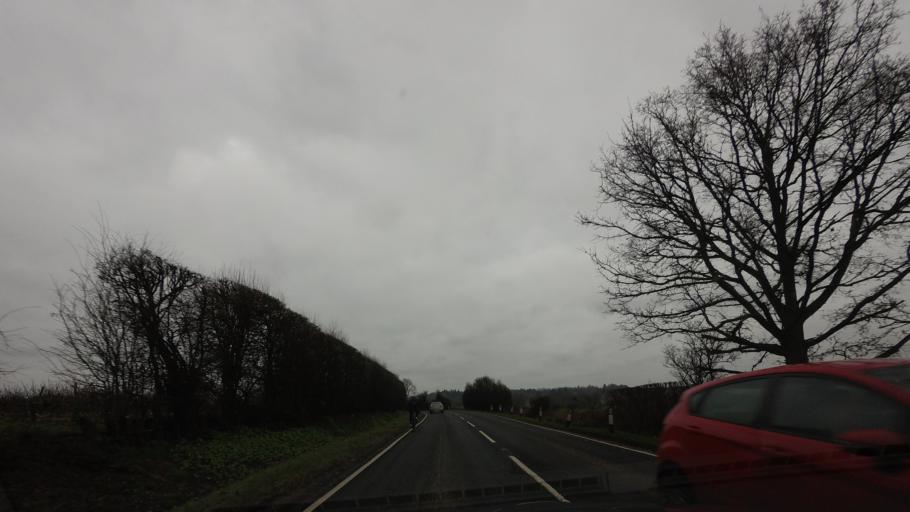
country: GB
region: England
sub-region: Kent
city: Marden
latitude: 51.2080
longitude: 0.5175
